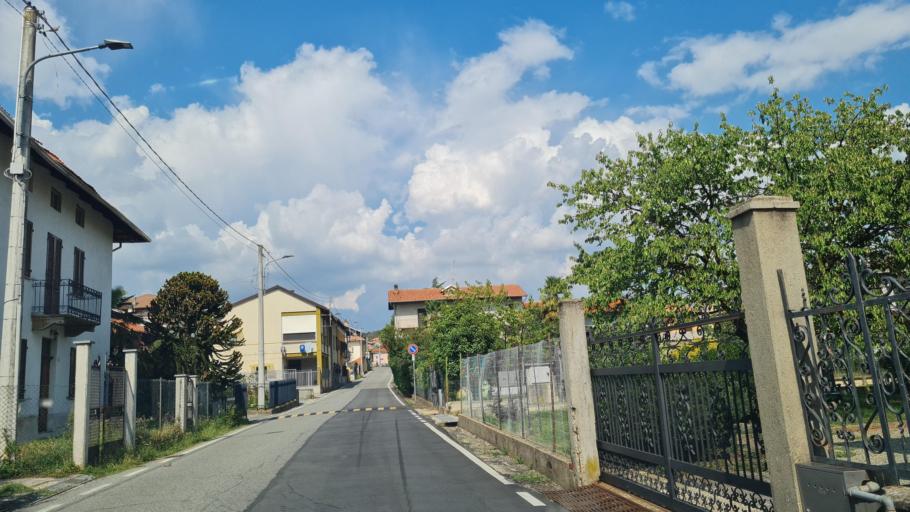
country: IT
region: Piedmont
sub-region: Provincia di Biella
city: Cossato
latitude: 45.5766
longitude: 8.1802
